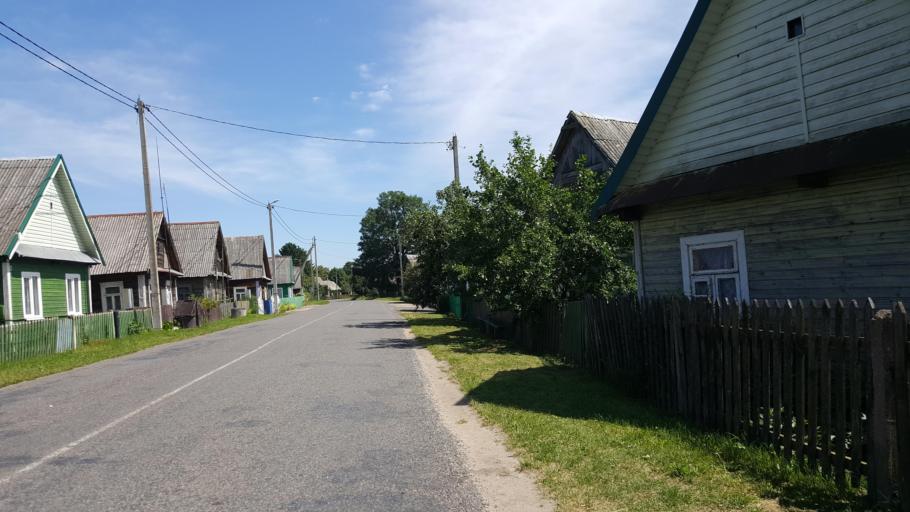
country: BY
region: Brest
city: Pruzhany
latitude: 52.5626
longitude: 24.2234
